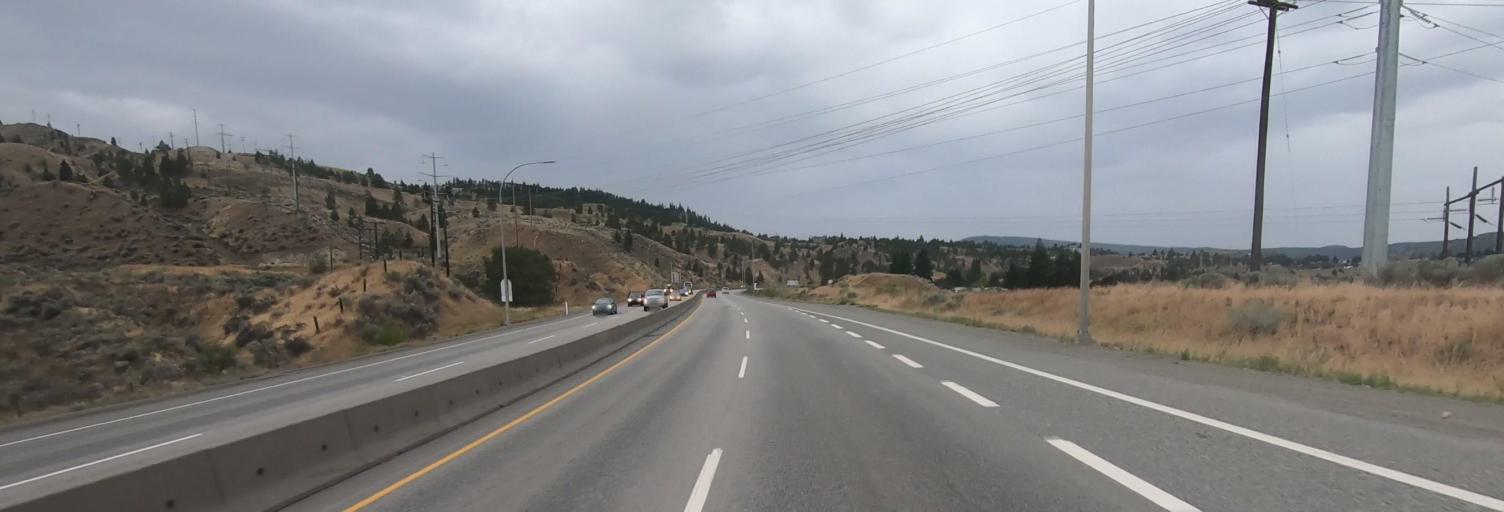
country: CA
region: British Columbia
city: Kamloops
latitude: 50.6653
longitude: -120.3119
